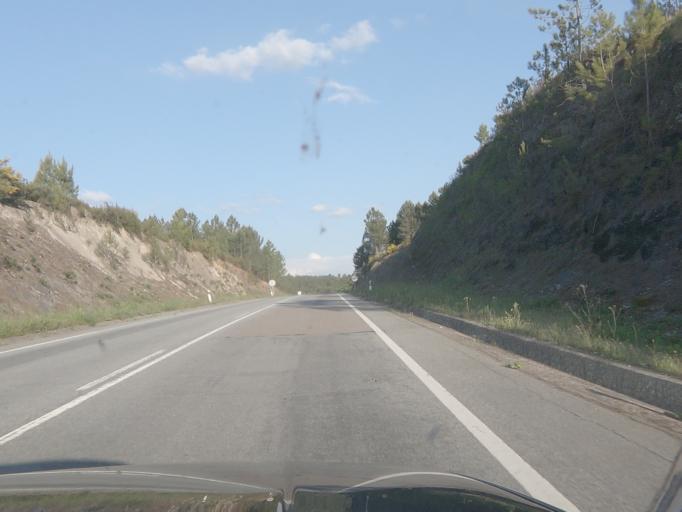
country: PT
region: Portalegre
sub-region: Marvao
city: Marvao
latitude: 39.3715
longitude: -7.3499
